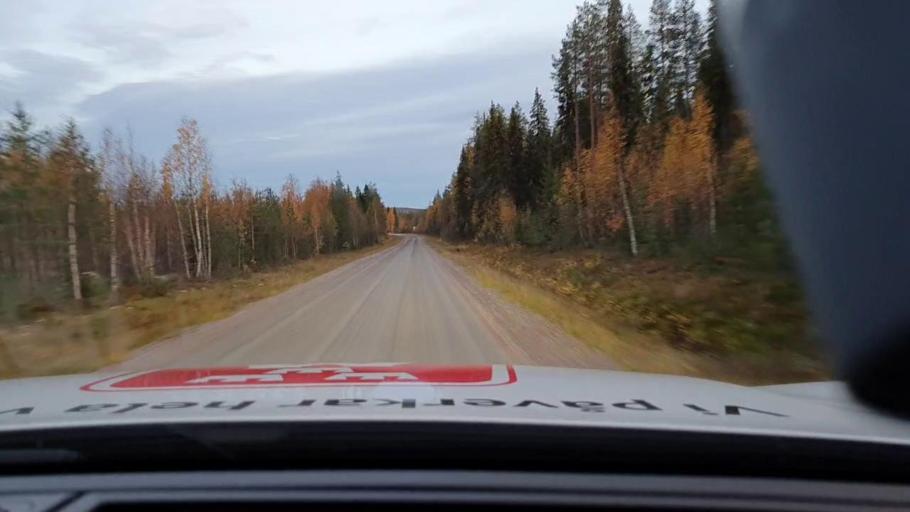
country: SE
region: Norrbotten
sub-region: Overkalix Kommun
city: OEverkalix
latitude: 66.2487
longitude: 23.2079
